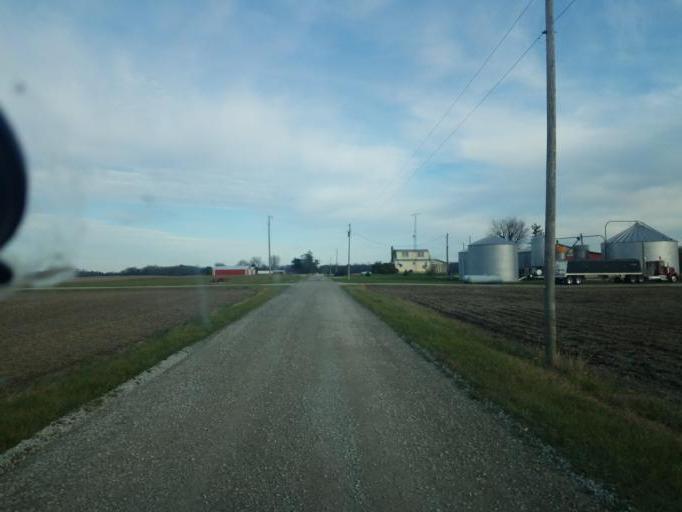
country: US
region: Ohio
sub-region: Morrow County
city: Mount Gilead
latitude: 40.6083
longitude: -82.8996
